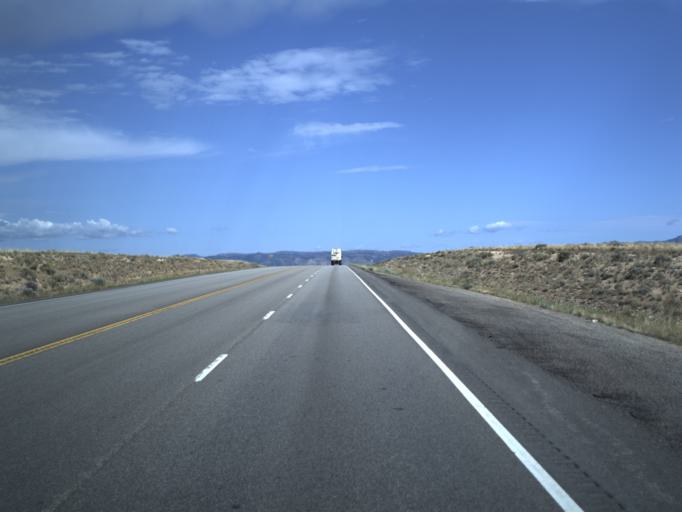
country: US
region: Utah
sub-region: Carbon County
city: East Carbon City
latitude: 39.5021
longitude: -110.5287
